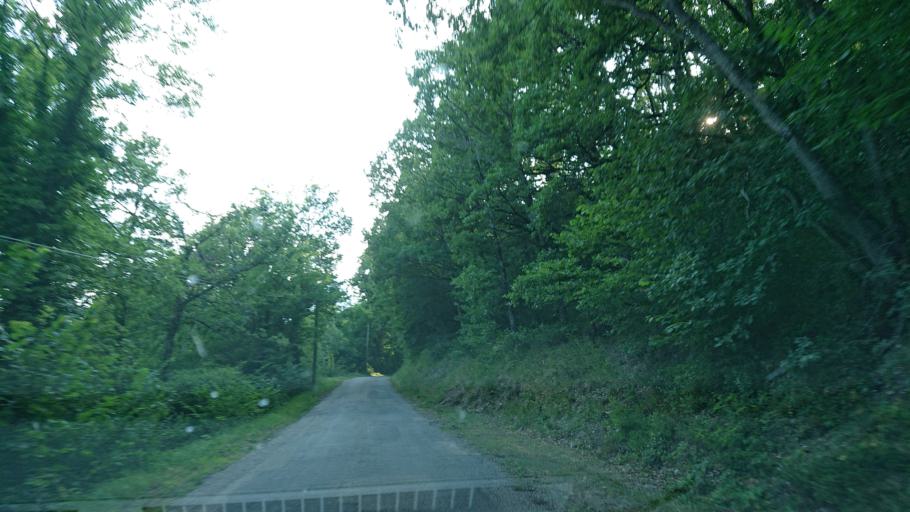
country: FR
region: Rhone-Alpes
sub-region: Departement de l'Isere
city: La Mure
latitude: 44.8164
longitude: 5.9396
